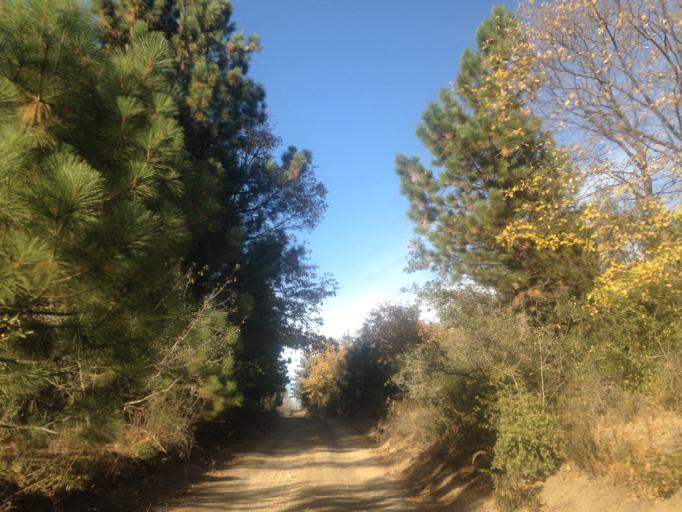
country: US
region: California
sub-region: San Bernardino County
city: Yucaipa
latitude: 34.1349
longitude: -117.0107
